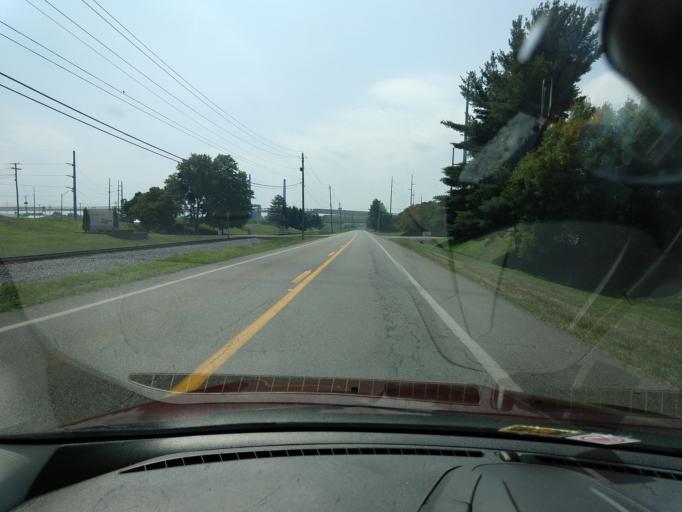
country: US
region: West Virginia
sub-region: Mason County
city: New Haven
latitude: 38.9772
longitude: -81.9412
